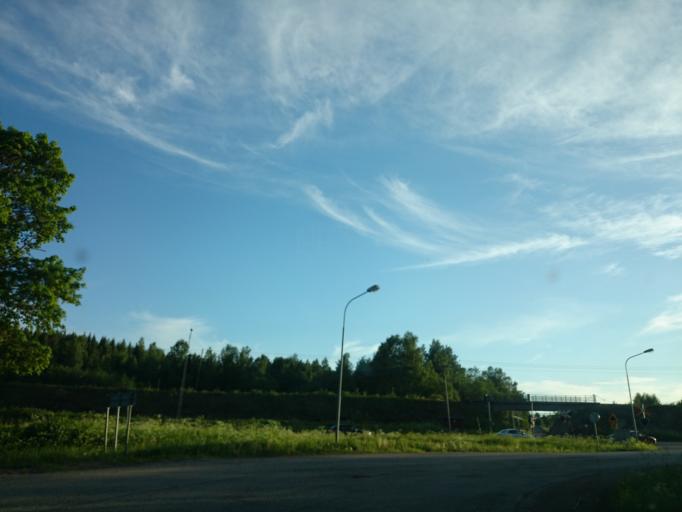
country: SE
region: Vaesternorrland
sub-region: Sundsvalls Kommun
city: Stockvik
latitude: 62.3323
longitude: 17.3635
